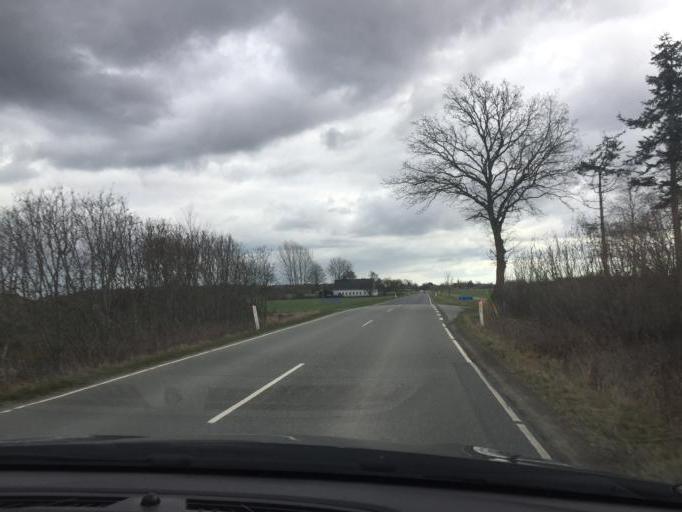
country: DK
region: South Denmark
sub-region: Kerteminde Kommune
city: Langeskov
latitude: 55.2988
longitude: 10.5994
